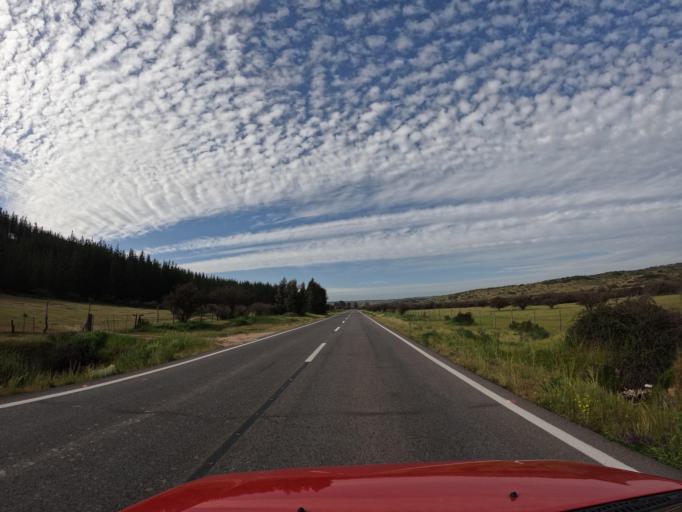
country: CL
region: O'Higgins
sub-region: Provincia de Colchagua
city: Santa Cruz
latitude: -34.3019
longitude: -71.7346
